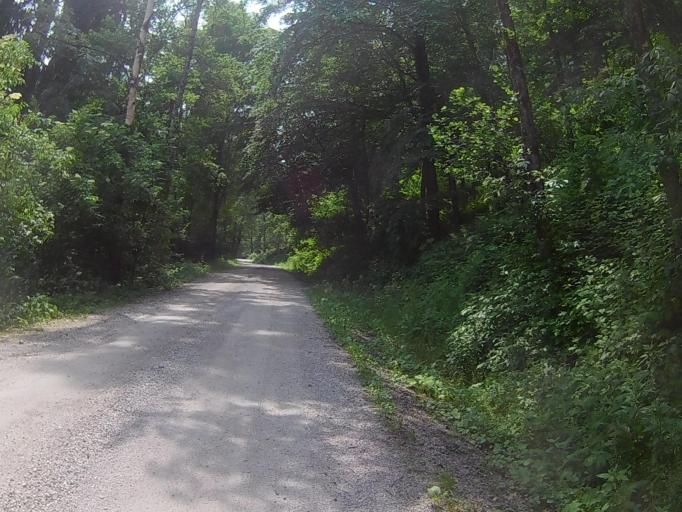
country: SI
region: Ruse
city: Bistrica ob Dravi
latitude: 46.5313
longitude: 15.5449
